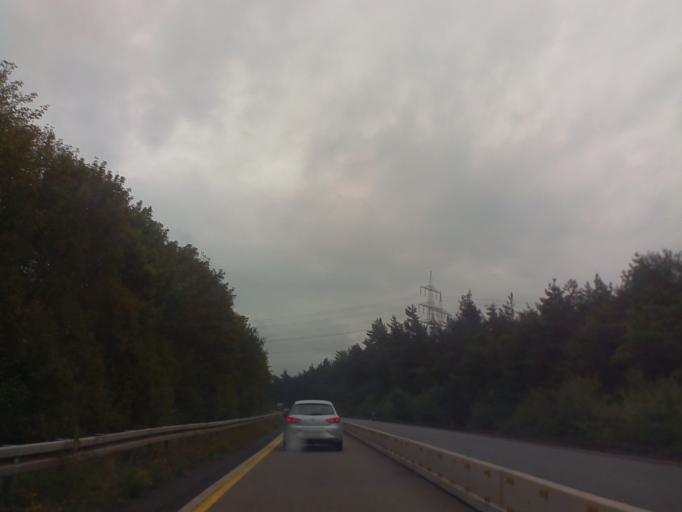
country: DE
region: Hesse
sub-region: Regierungsbezirk Darmstadt
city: Grosskrotzenburg
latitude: 50.1078
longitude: 8.9979
